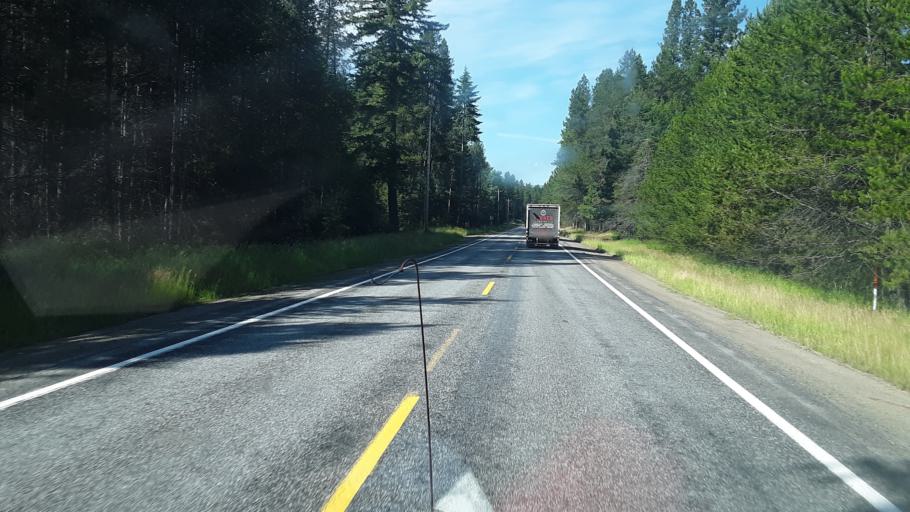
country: US
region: Idaho
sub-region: Boundary County
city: Bonners Ferry
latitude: 48.5310
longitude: -116.4275
